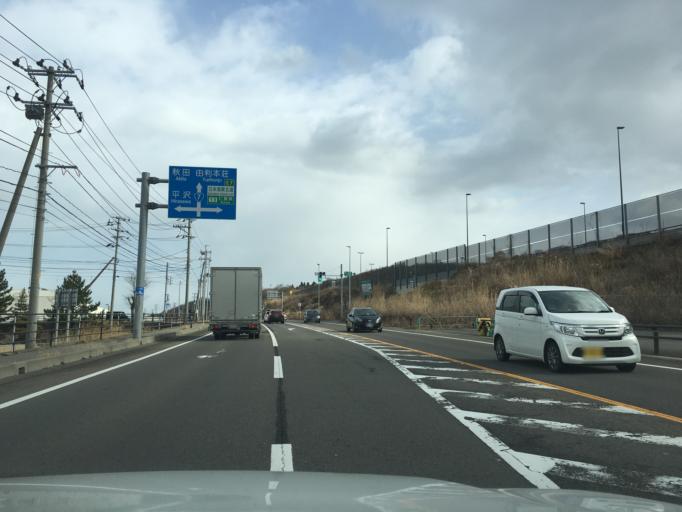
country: JP
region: Yamagata
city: Yuza
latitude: 39.2919
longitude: 139.9746
